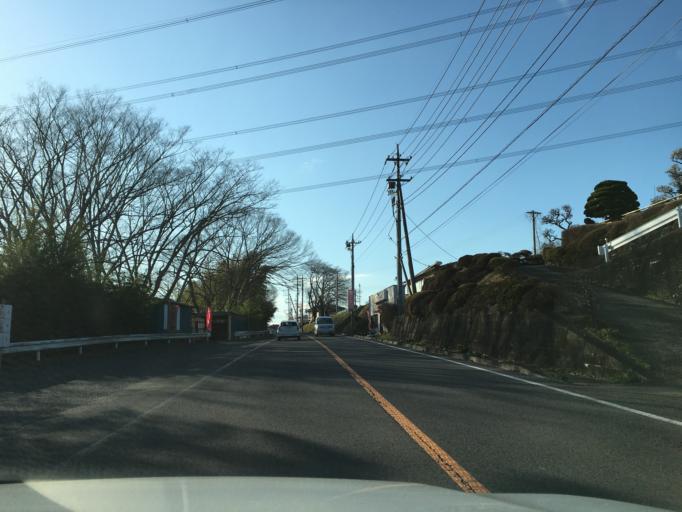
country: JP
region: Ibaraki
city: Daigo
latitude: 36.7767
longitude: 140.3296
